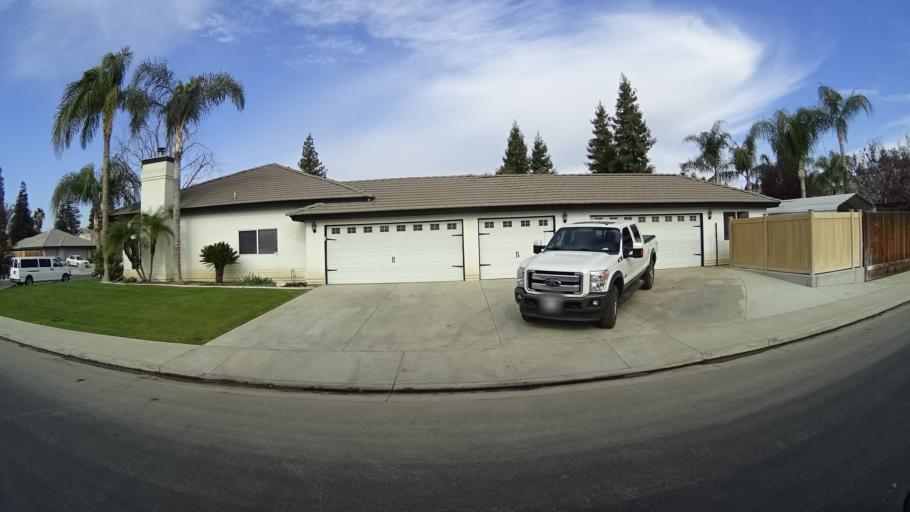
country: US
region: California
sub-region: Kern County
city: Greenacres
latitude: 35.3982
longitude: -119.0783
